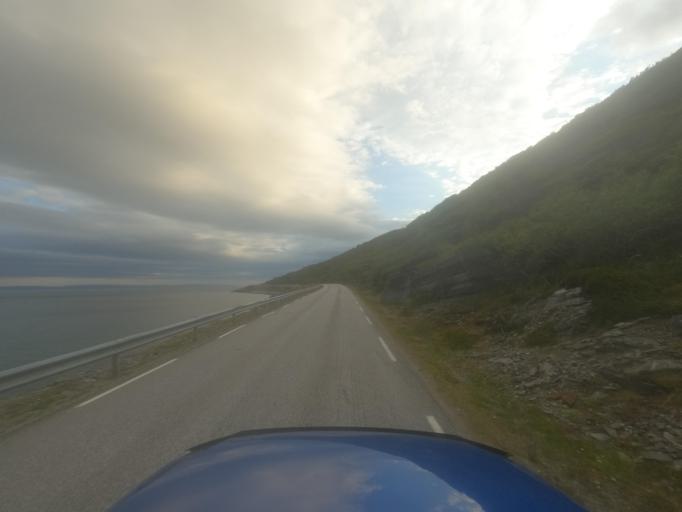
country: NO
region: Finnmark Fylke
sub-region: Nordkapp
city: Honningsvag
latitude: 70.6897
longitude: 25.4945
